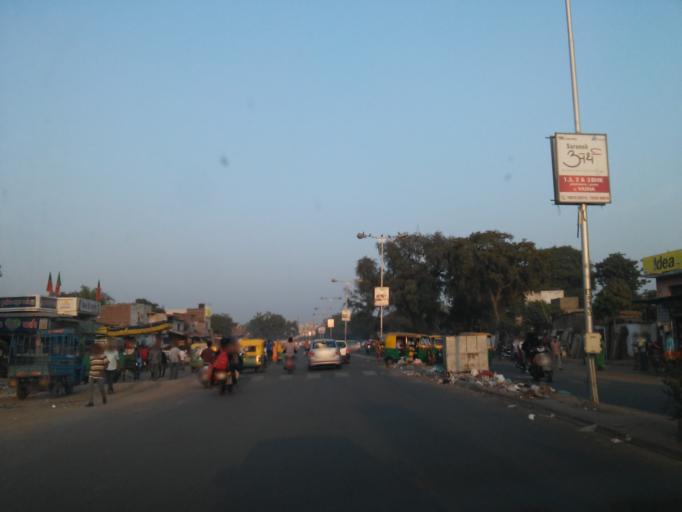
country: IN
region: Gujarat
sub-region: Ahmadabad
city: Sarkhej
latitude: 22.9969
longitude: 72.5389
